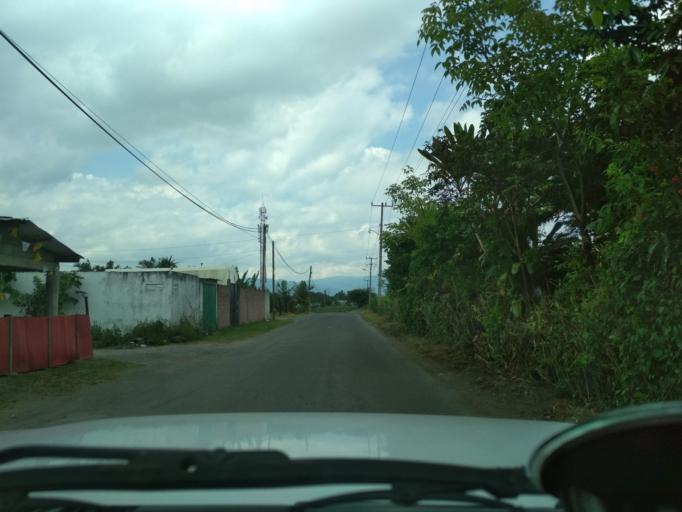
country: MX
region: Veracruz
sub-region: Ixtaczoquitlan
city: Buenavista
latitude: 18.9019
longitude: -97.0287
